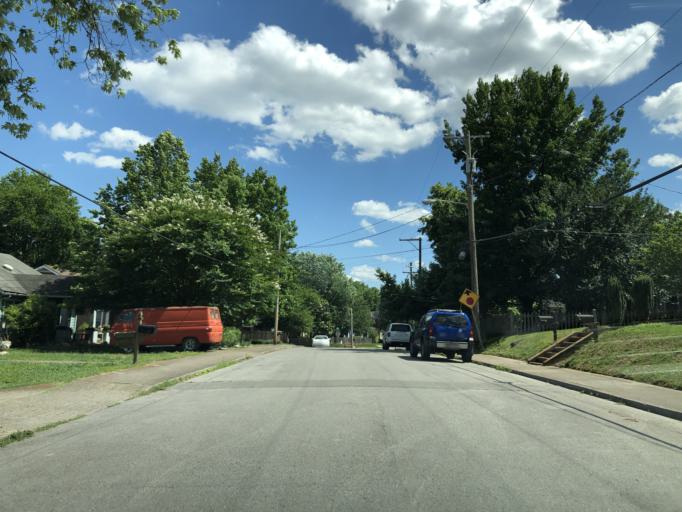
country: US
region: Tennessee
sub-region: Davidson County
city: Nashville
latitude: 36.1850
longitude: -86.7381
